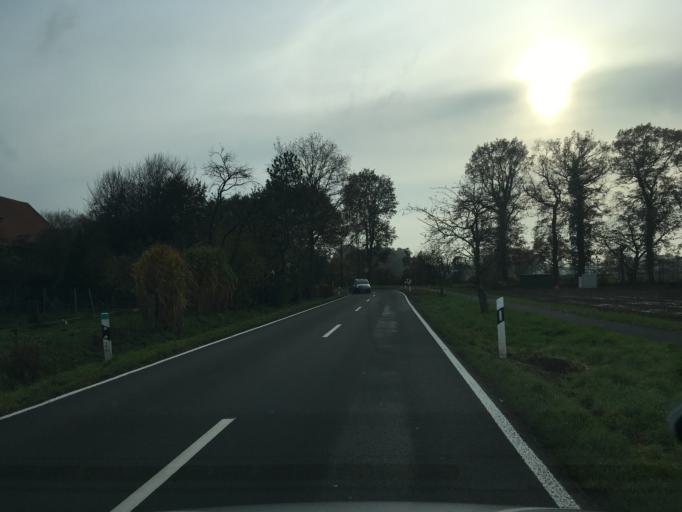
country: DE
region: North Rhine-Westphalia
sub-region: Regierungsbezirk Munster
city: Velen
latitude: 51.9327
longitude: 6.9457
